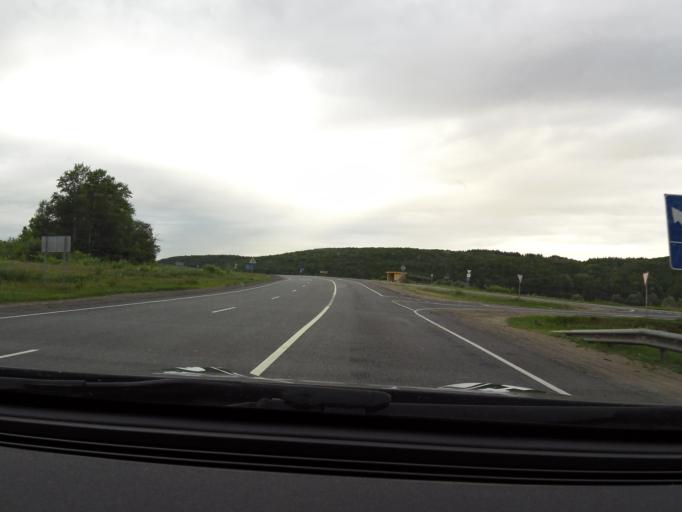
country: RU
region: Chuvashia
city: Kozlovka
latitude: 55.7834
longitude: 48.1925
